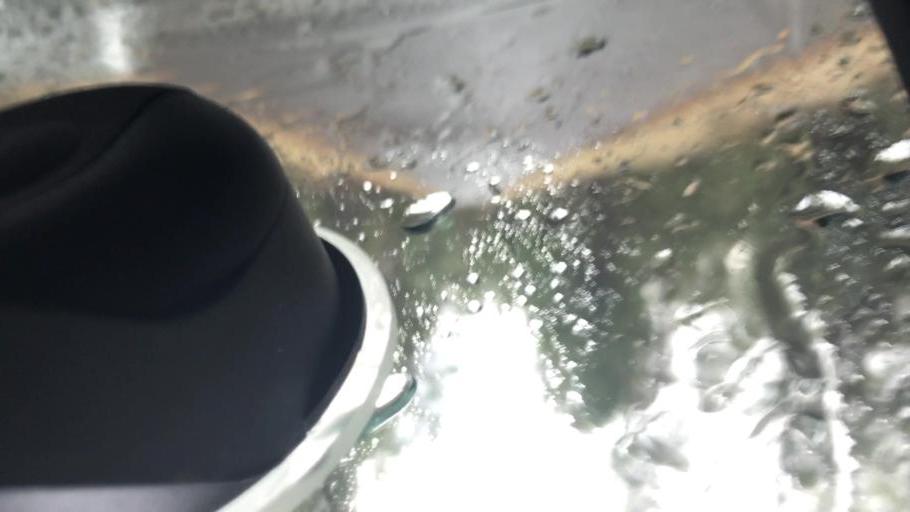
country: US
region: Arizona
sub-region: Yavapai County
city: Prescott
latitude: 34.5080
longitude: -112.3805
